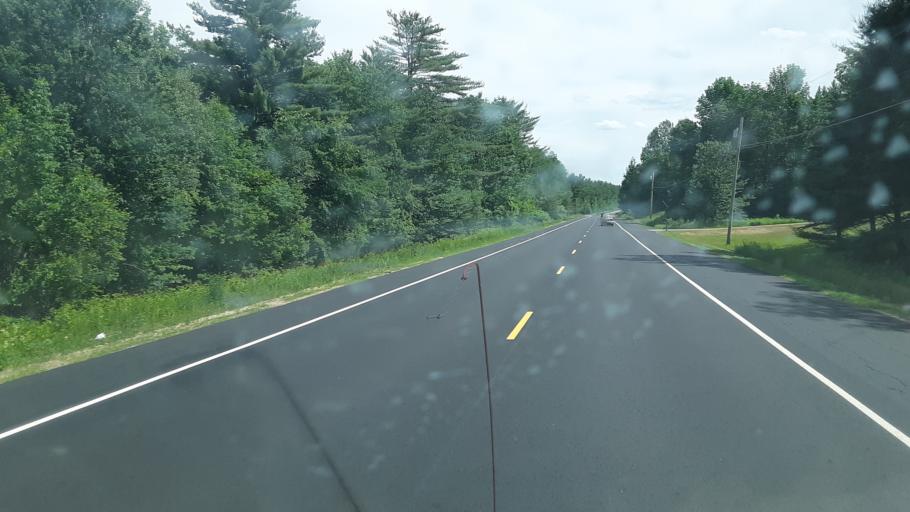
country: US
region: Maine
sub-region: Somerset County
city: Norridgewock
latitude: 44.6610
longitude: -69.7058
